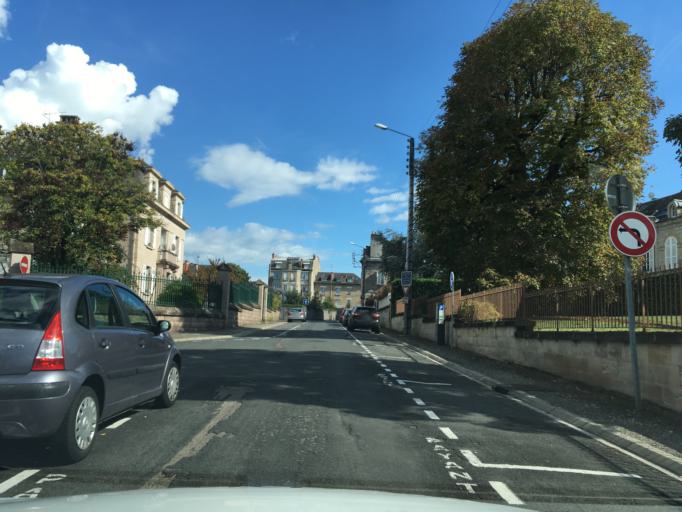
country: FR
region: Limousin
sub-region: Departement de la Correze
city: Brive-la-Gaillarde
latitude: 45.1542
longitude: 1.5271
